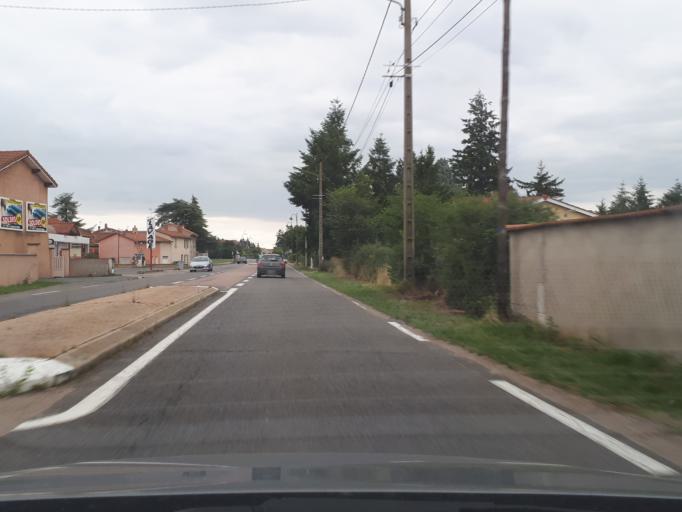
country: FR
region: Rhone-Alpes
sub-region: Departement de la Loire
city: Montrond-les-Bains
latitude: 45.6358
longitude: 4.2383
